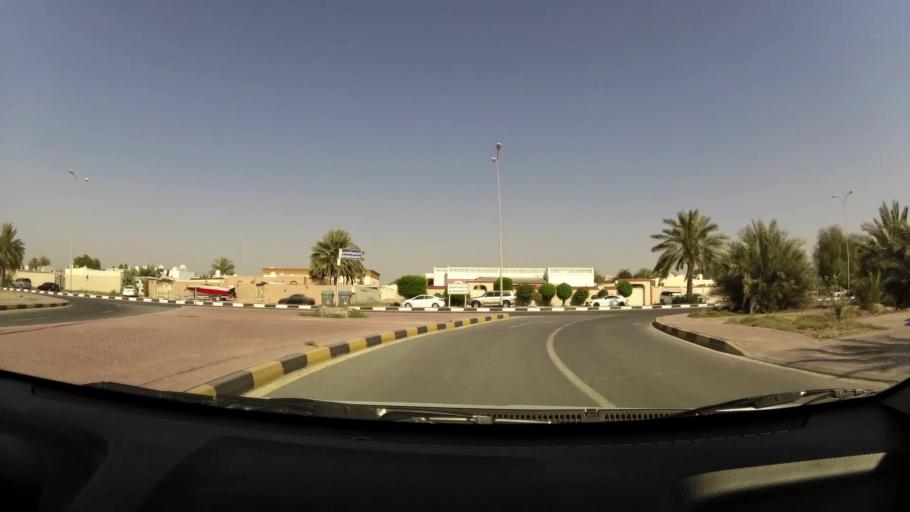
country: AE
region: Ajman
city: Ajman
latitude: 25.4108
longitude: 55.4702
